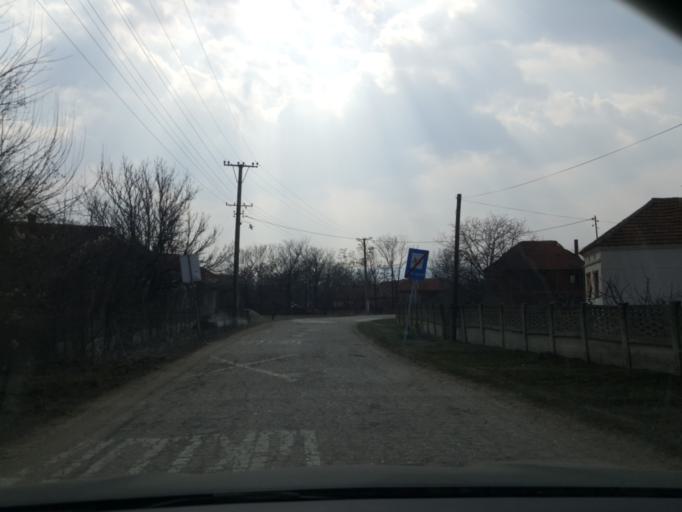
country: RS
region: Central Serbia
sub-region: Nisavski Okrug
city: Aleksinac
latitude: 43.4485
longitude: 21.7893
